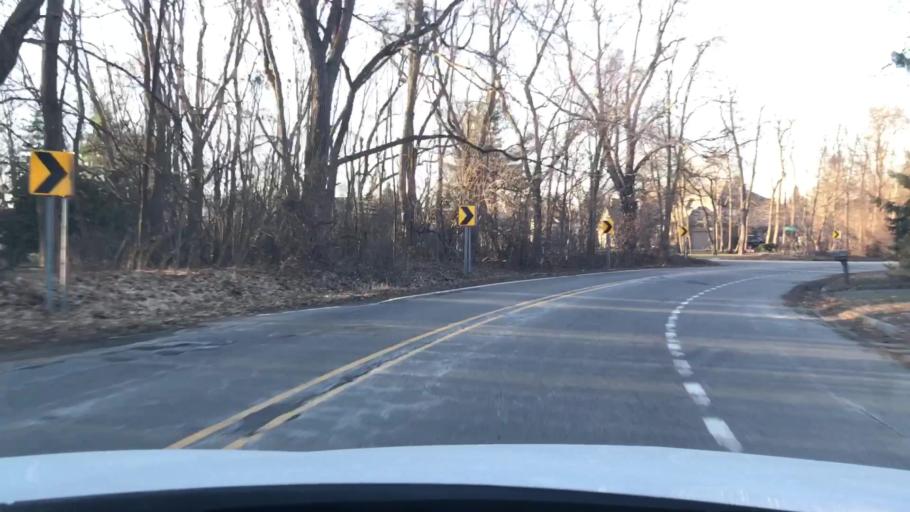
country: US
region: Michigan
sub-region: Oakland County
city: West Bloomfield Township
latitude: 42.5932
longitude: -83.4021
